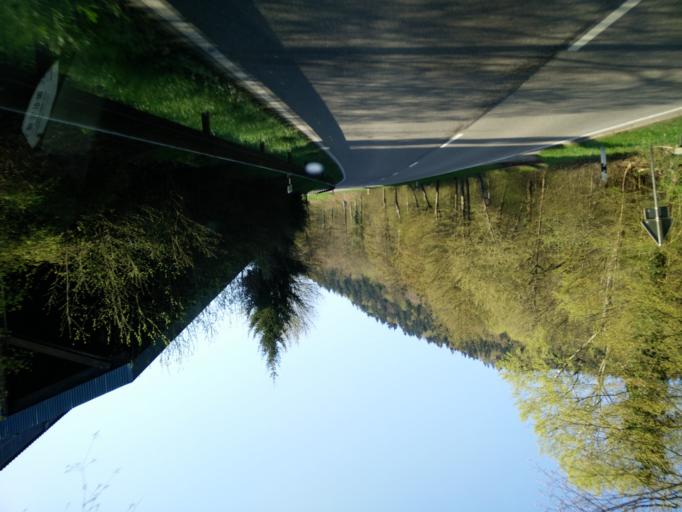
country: DE
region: Baden-Wuerttemberg
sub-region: Karlsruhe Region
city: Bad Liebenzell
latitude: 48.7896
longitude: 8.7252
